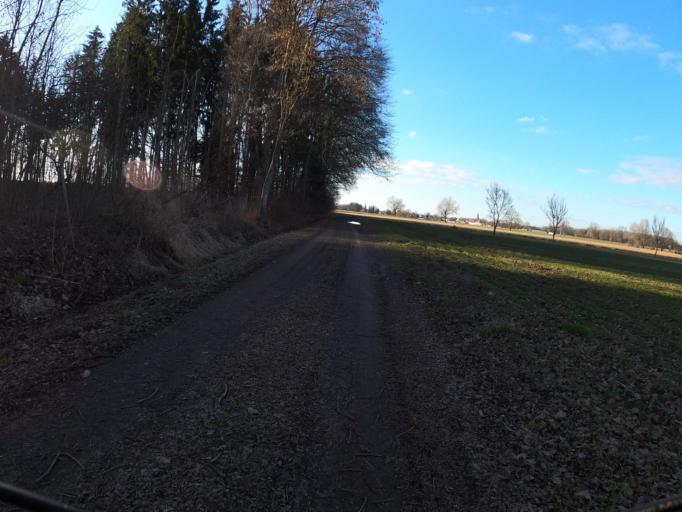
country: DE
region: Bavaria
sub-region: Swabia
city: Leipheim
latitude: 48.4188
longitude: 10.2026
